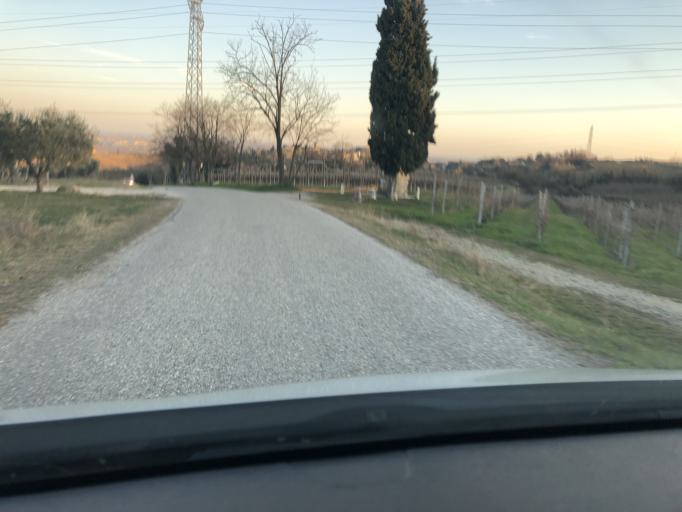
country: IT
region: Veneto
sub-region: Provincia di Verona
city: Sandra
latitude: 45.4631
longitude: 10.8096
